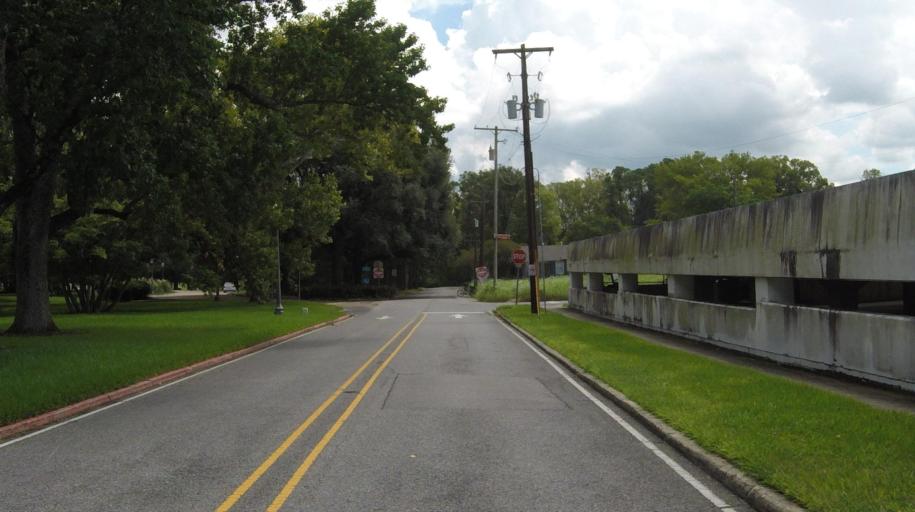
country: US
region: Louisiana
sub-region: West Baton Rouge Parish
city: Port Allen
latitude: 30.4568
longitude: -91.1853
